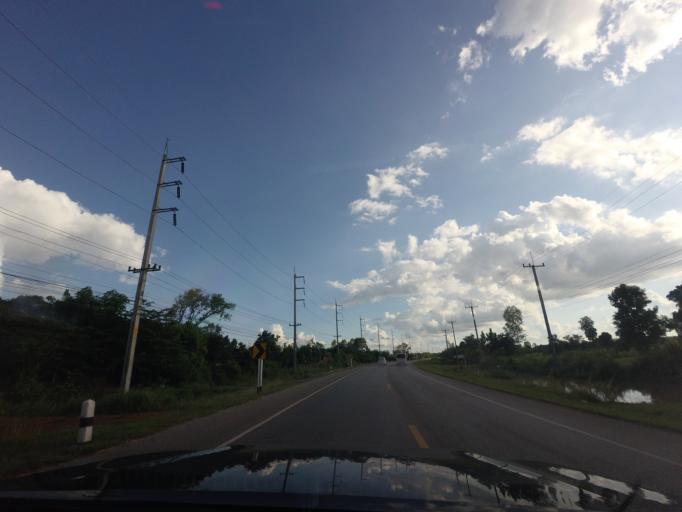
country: TH
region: Changwat Udon Thani
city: Thung Fon
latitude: 17.5009
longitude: 103.2034
